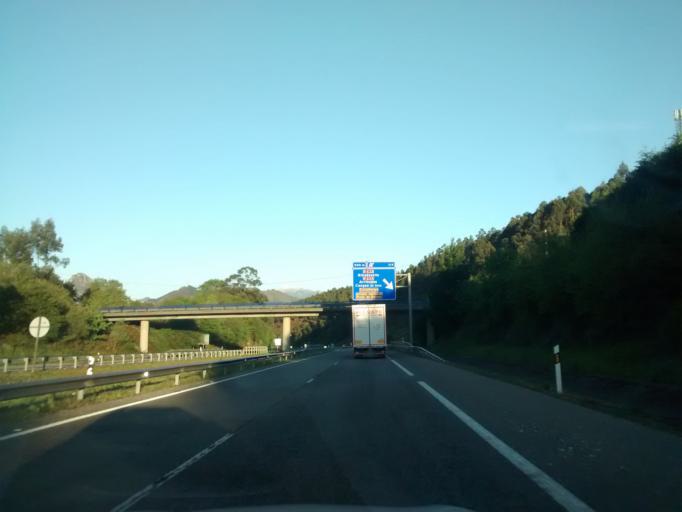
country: ES
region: Asturias
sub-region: Province of Asturias
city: Ribadesella
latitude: 43.4399
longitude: -5.0307
